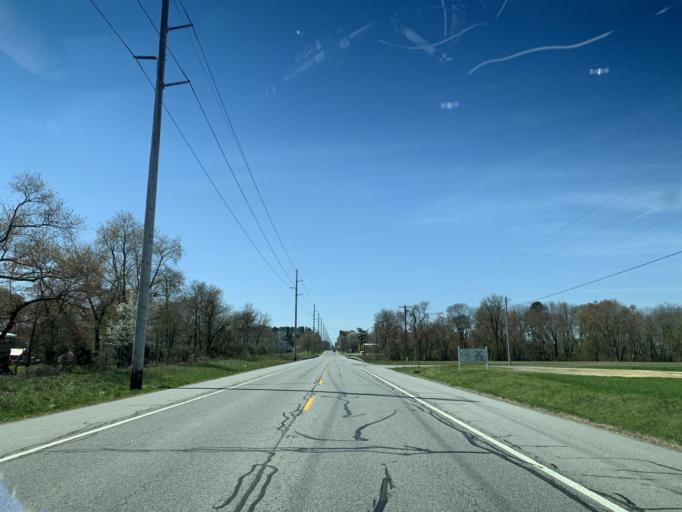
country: US
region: Maryland
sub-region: Caroline County
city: Ridgely
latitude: 38.8820
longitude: -75.9904
